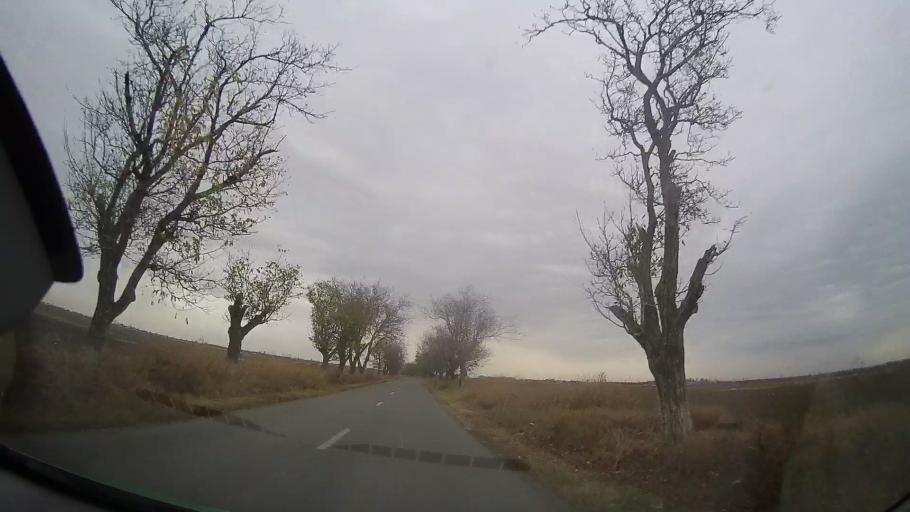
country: RO
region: Prahova
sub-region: Oras Mizil
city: Mizil
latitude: 45.0107
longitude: 26.4152
